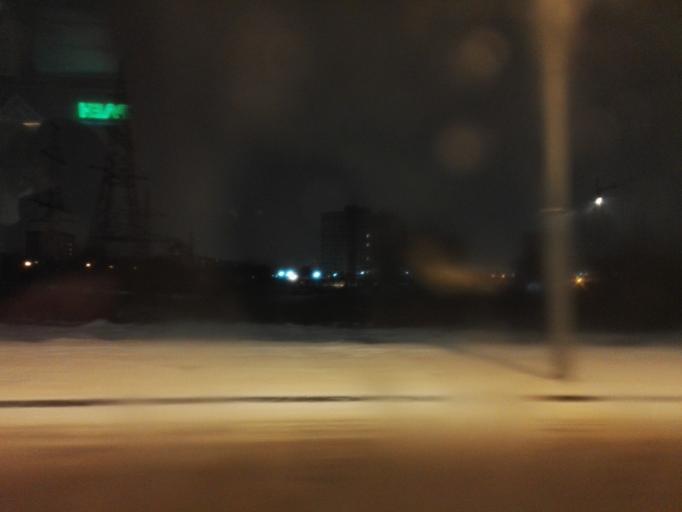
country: RU
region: Tula
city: Tula
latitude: 54.1791
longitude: 37.6467
